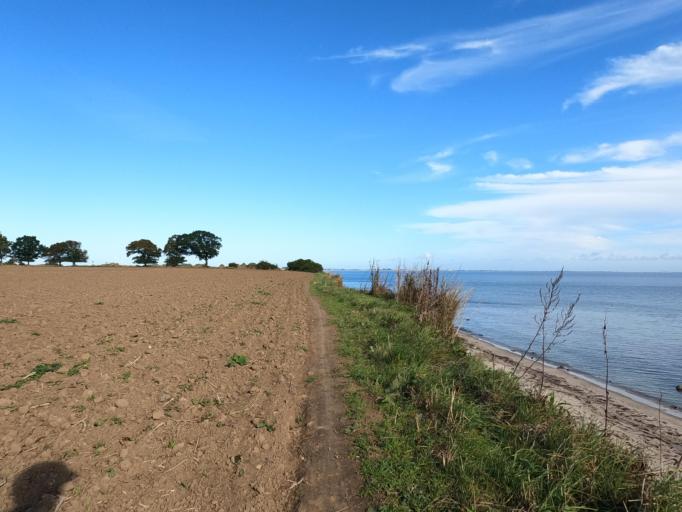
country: DE
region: Schleswig-Holstein
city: Dahme
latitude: 54.2865
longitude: 11.0812
